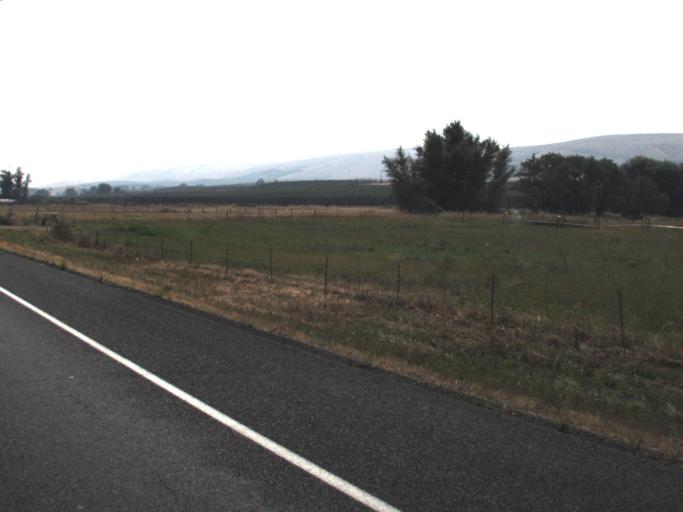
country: US
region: Washington
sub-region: Yakima County
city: Terrace Heights
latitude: 46.5471
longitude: -120.3300
